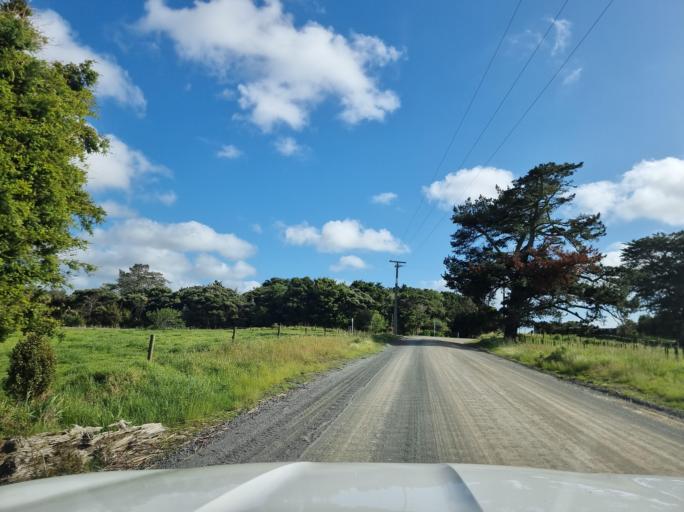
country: NZ
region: Auckland
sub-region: Auckland
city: Wellsford
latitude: -36.1277
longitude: 174.5939
